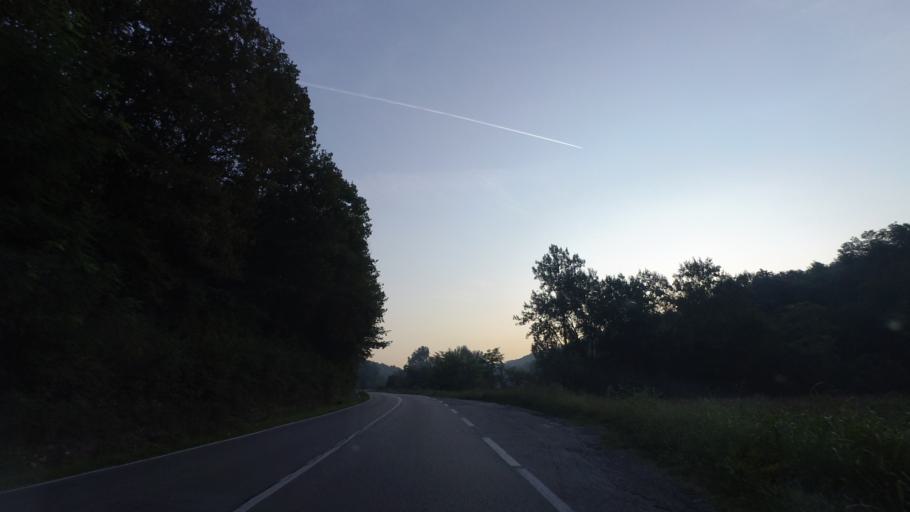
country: HR
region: Brodsko-Posavska
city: Cernik
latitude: 45.3140
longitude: 17.4367
